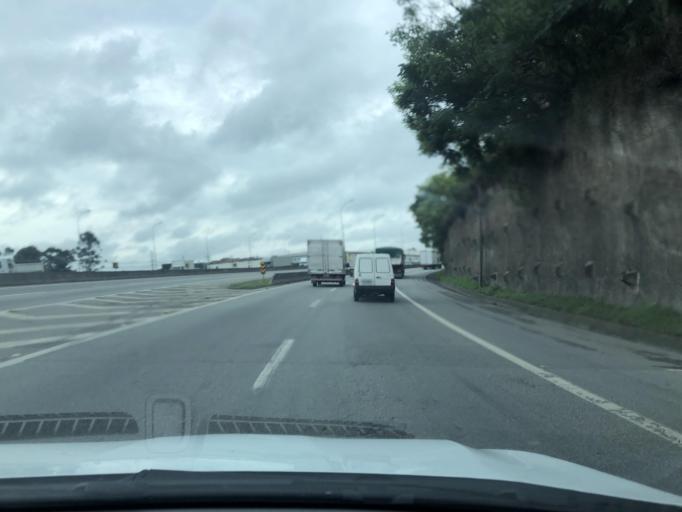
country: BR
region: Sao Paulo
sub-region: Embu
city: Embu
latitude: -23.6376
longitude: -46.8331
